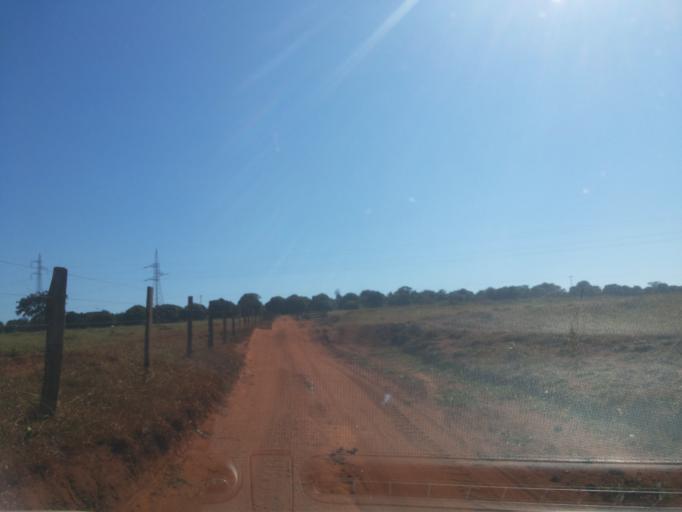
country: BR
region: Minas Gerais
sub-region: Centralina
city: Centralina
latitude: -18.7280
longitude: -49.1784
